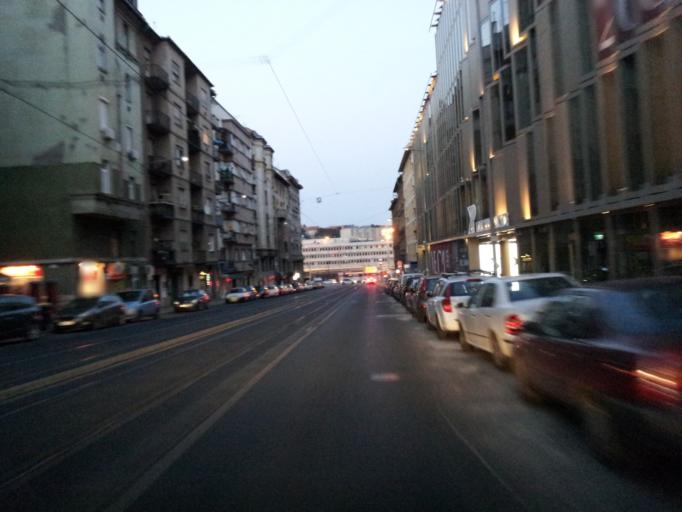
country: HU
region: Budapest
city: Budapest XII. keruelet
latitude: 47.4982
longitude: 19.0218
